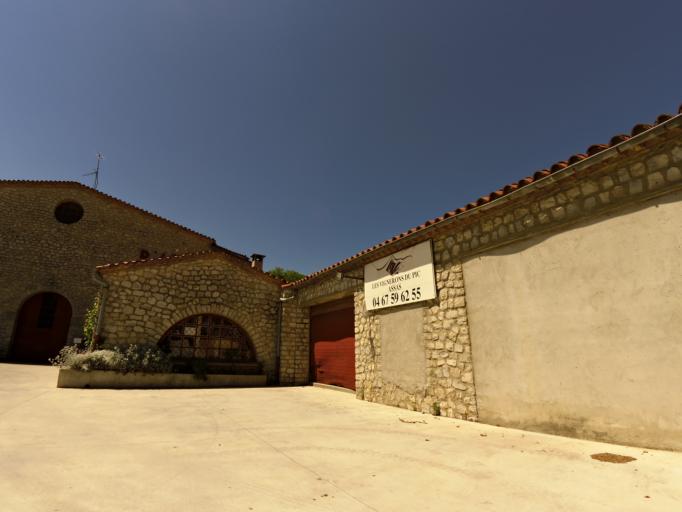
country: FR
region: Languedoc-Roussillon
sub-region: Departement de l'Herault
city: Assas
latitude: 43.7056
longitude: 3.9008
